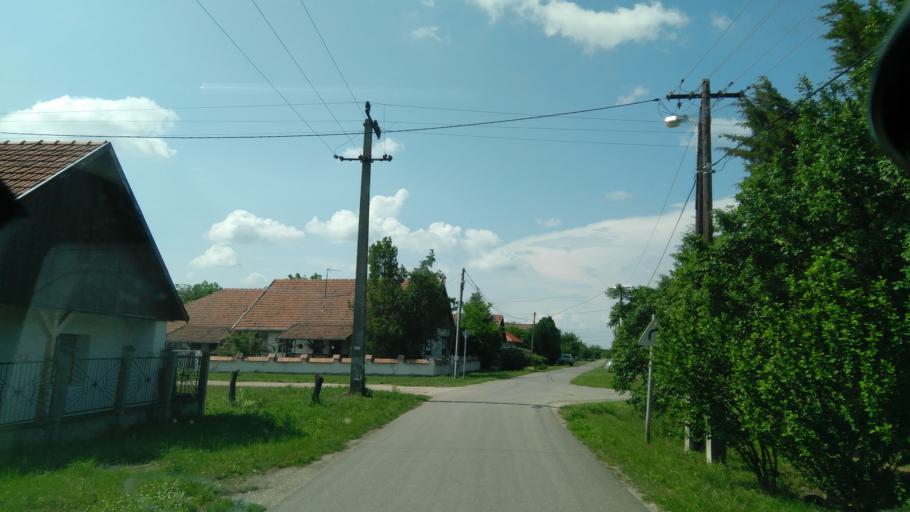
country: HU
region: Bekes
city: Doboz
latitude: 46.7363
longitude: 21.2297
